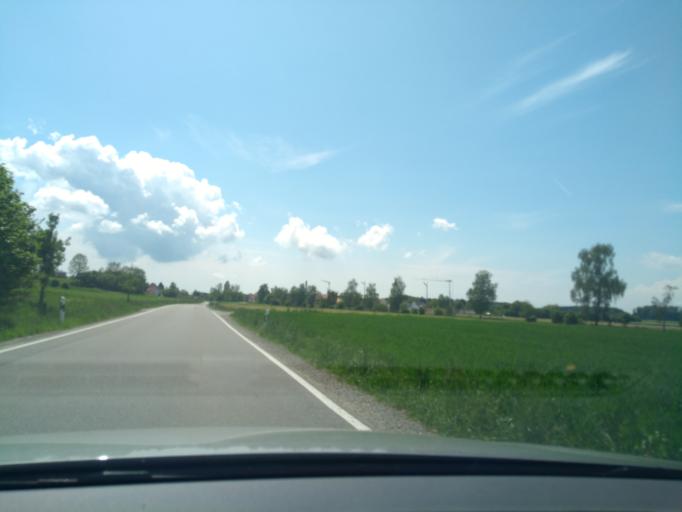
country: DE
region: Baden-Wuerttemberg
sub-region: Tuebingen Region
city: Bad Waldsee
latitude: 47.9274
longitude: 9.8069
